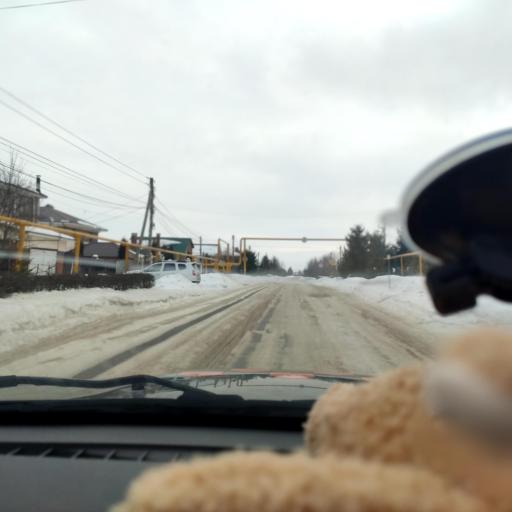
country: RU
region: Samara
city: Podstepki
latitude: 53.5185
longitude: 49.1810
